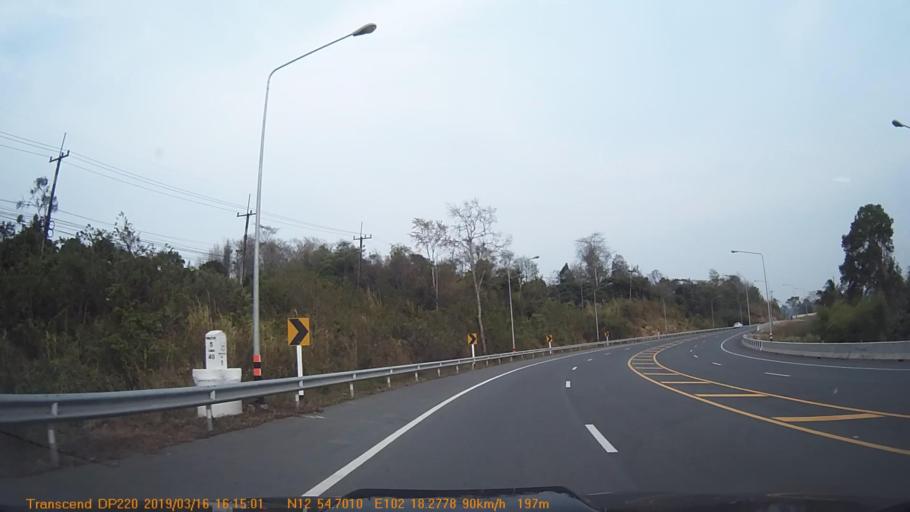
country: TH
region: Chanthaburi
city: Pong Nam Ron
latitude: 12.9116
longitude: 102.3049
